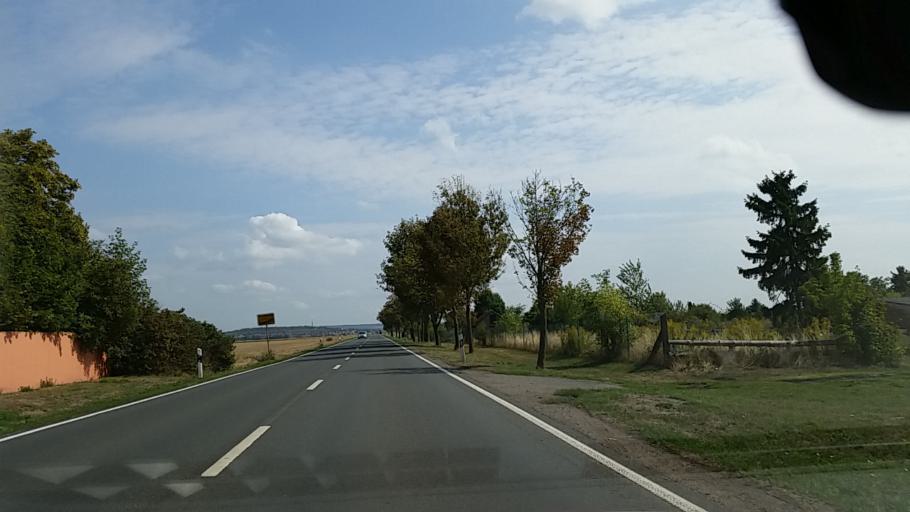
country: DE
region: Thuringia
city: Ringleben
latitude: 51.3679
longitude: 11.2296
